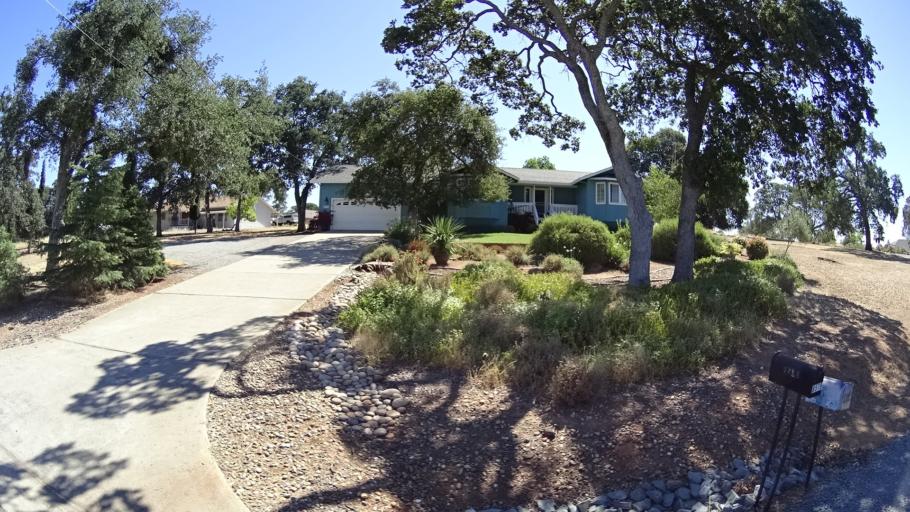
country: US
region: California
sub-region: Calaveras County
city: Rancho Calaveras
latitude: 38.1072
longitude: -120.8723
